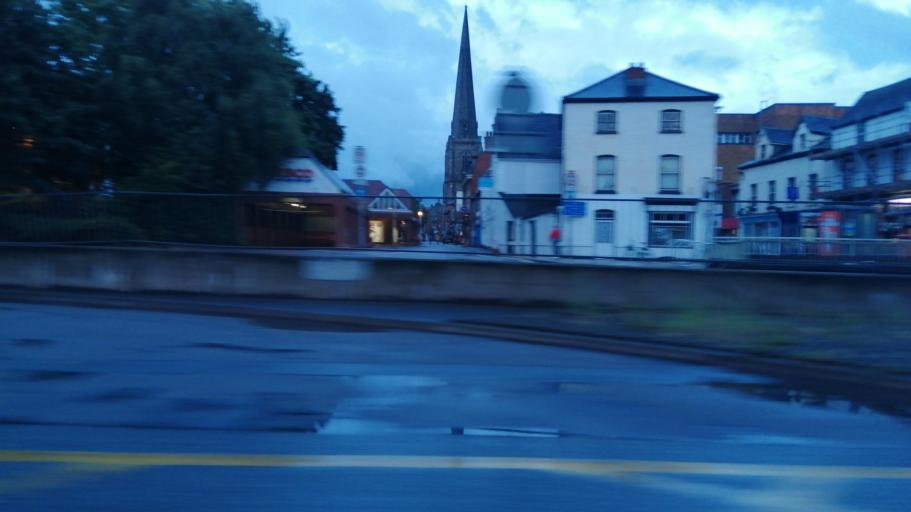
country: GB
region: England
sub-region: Herefordshire
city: Hereford
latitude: 52.0567
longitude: -2.7206
